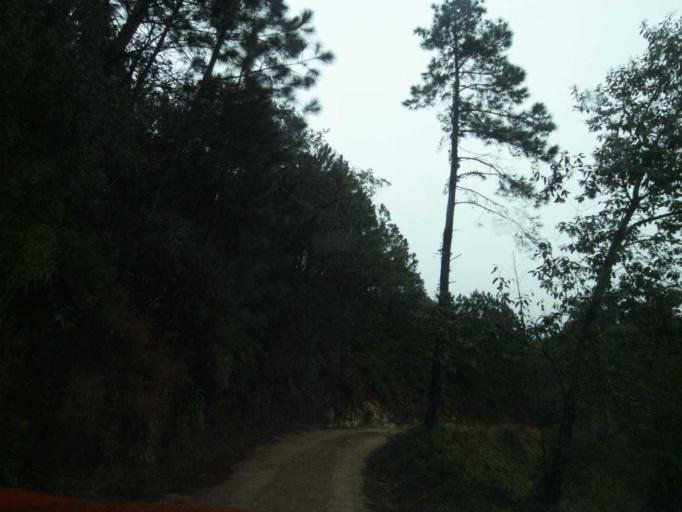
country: BR
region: Santa Catarina
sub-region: Anitapolis
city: Anitapolis
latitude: -27.9211
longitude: -49.1996
